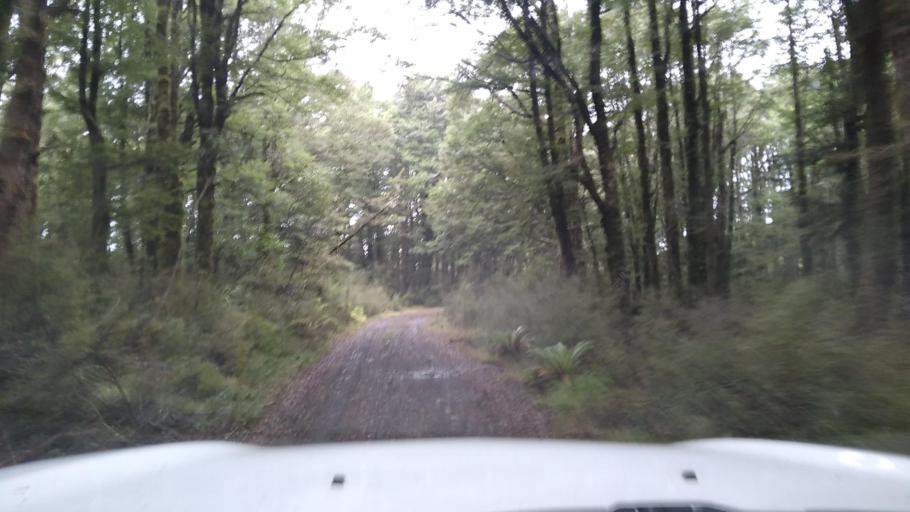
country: NZ
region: Manawatu-Wanganui
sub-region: Ruapehu District
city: Waiouru
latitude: -39.4103
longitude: 175.4839
